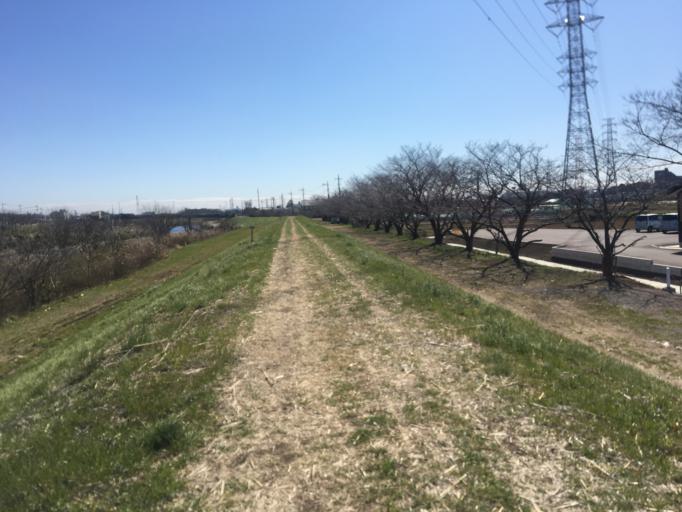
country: JP
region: Saitama
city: Asaka
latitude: 35.8224
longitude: 139.6035
